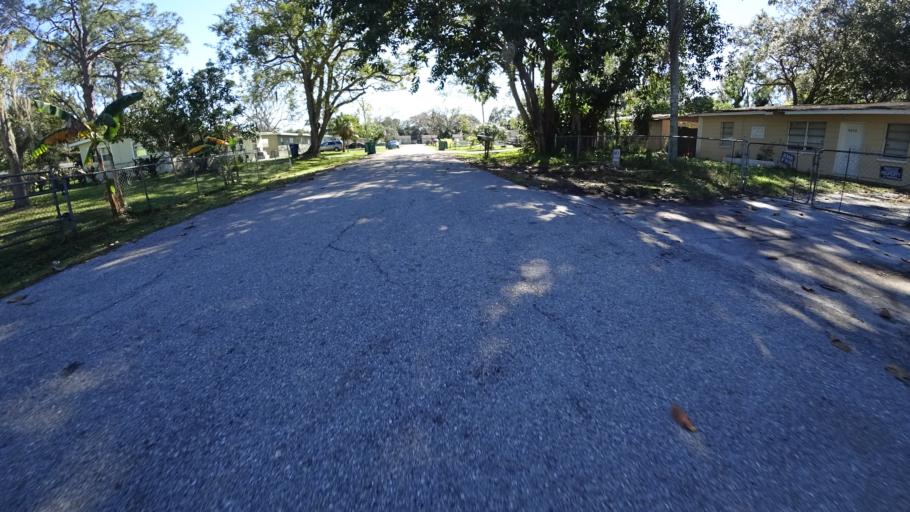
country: US
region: Florida
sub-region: Manatee County
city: Whitfield
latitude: 27.4343
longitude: -82.5543
